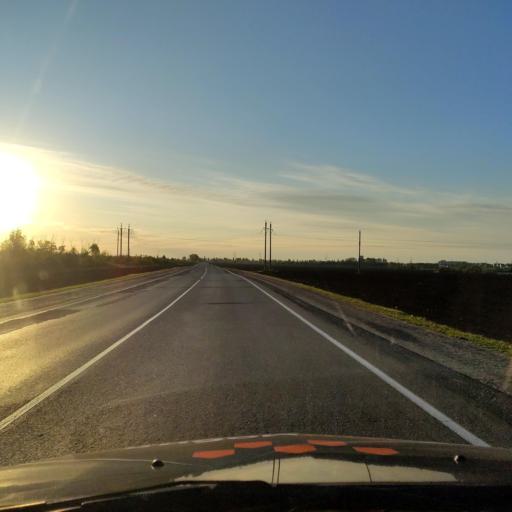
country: RU
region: Orjol
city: Livny
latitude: 52.4406
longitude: 37.5527
